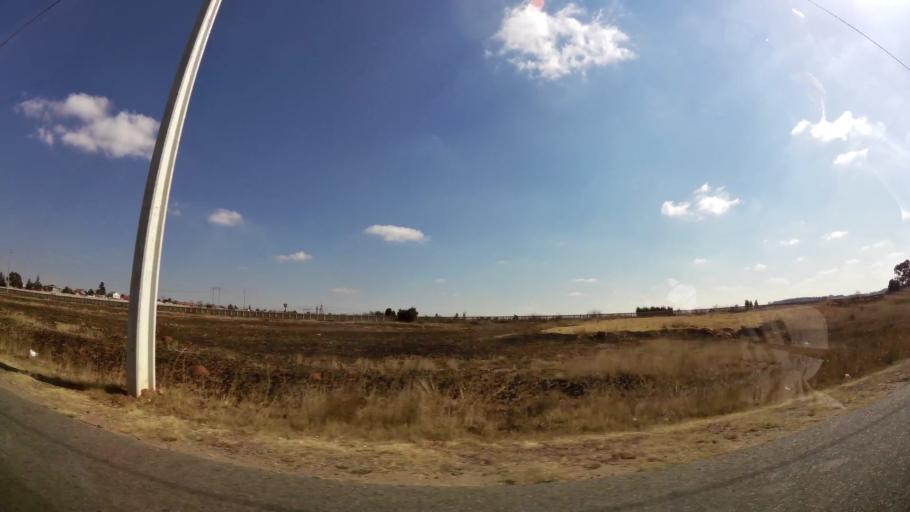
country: ZA
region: Gauteng
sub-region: West Rand District Municipality
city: Randfontein
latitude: -26.1614
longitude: 27.7617
